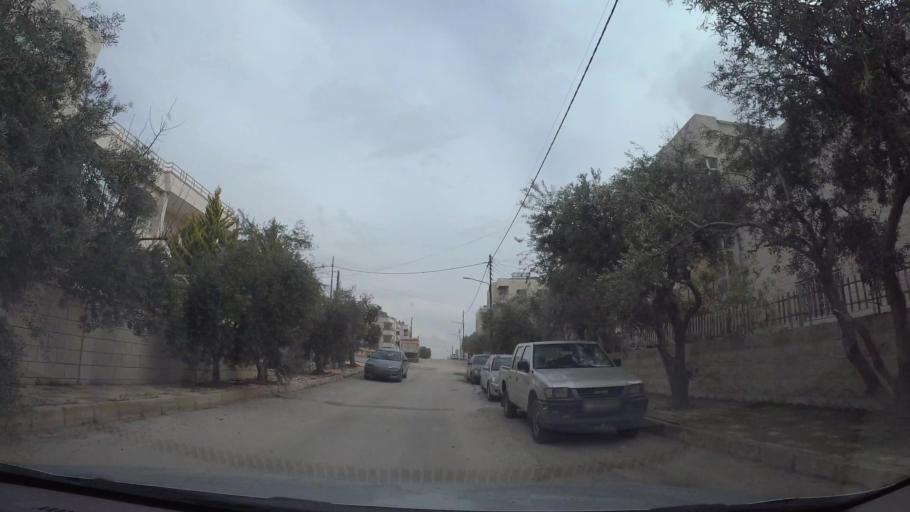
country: JO
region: Amman
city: Umm as Summaq
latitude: 31.8958
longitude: 35.8661
